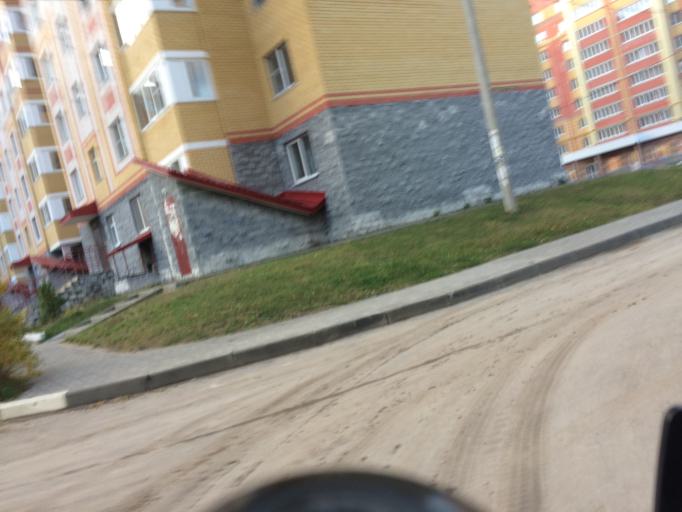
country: RU
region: Mariy-El
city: Yoshkar-Ola
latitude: 56.6379
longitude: 47.9303
